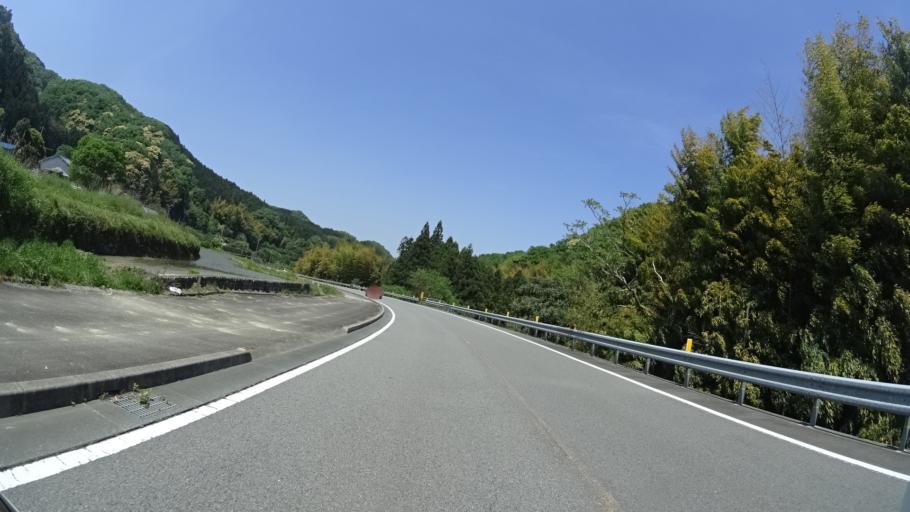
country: JP
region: Ehime
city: Hojo
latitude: 33.9777
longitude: 132.9045
